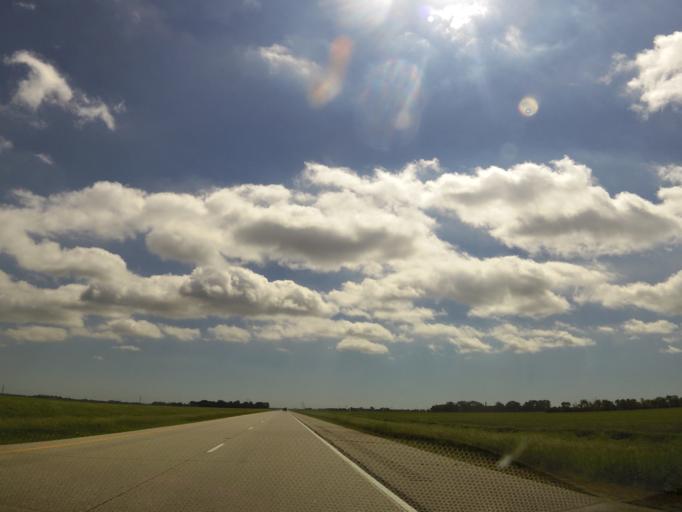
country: US
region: Minnesota
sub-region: Polk County
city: Crookston
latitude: 47.8035
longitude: -96.7537
